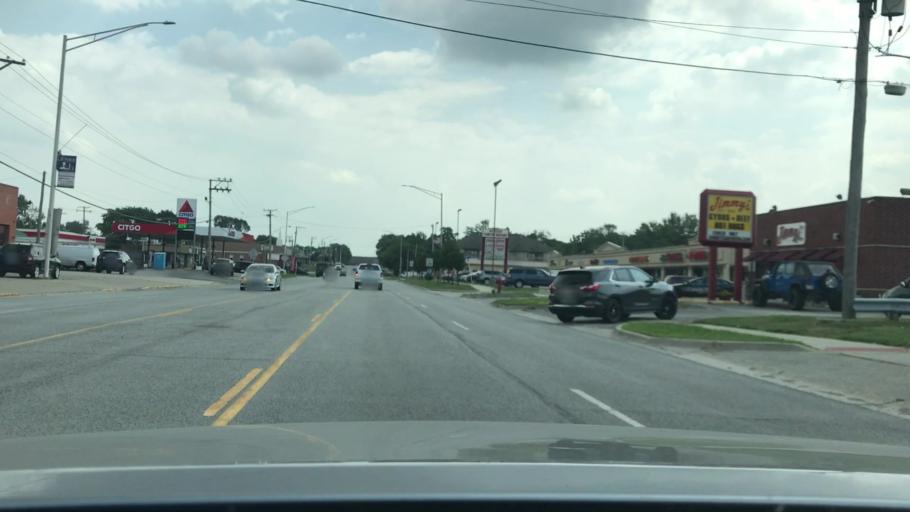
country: US
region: Illinois
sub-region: Cook County
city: Hickory Hills
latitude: 41.7401
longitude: -87.8189
